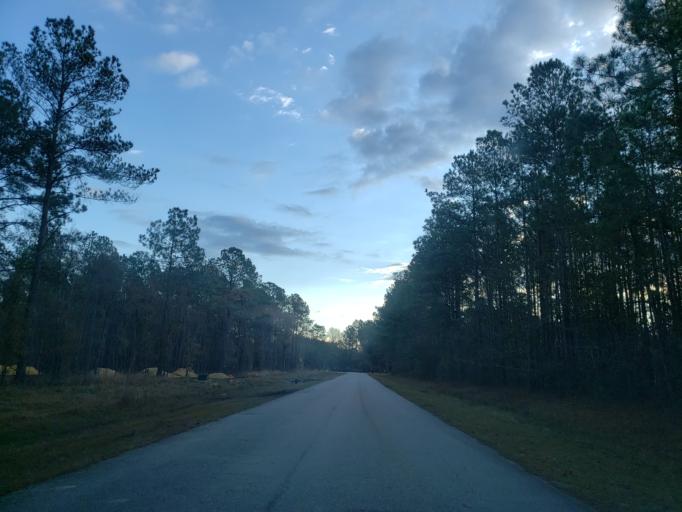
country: US
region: Georgia
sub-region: Chatham County
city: Bloomingdale
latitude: 32.1300
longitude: -81.3145
